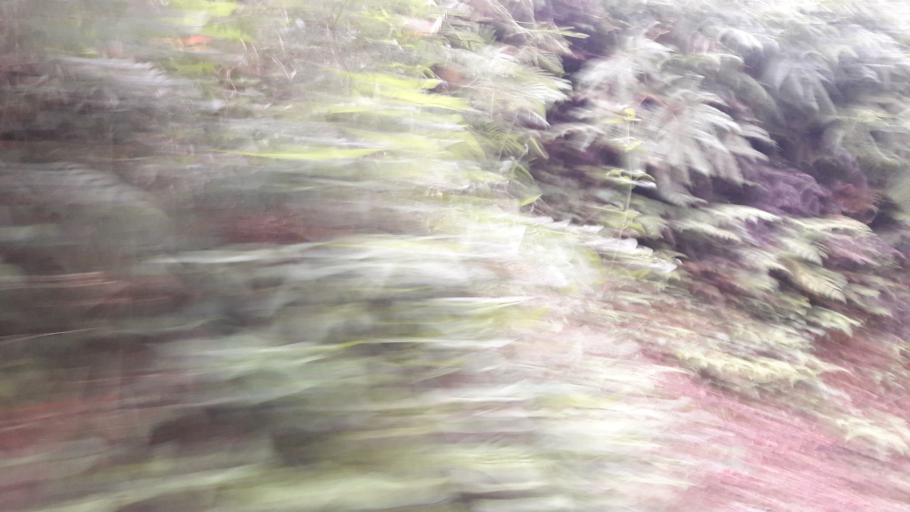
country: ID
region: West Java
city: Cipeundeuy
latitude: -6.6772
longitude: 106.5170
